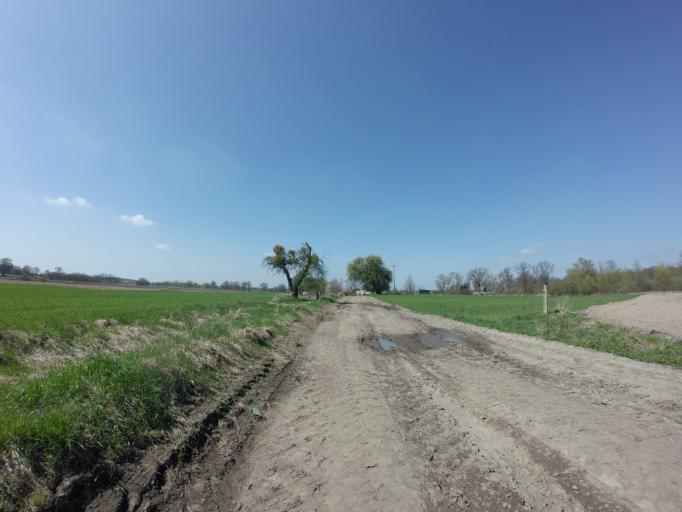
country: PL
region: West Pomeranian Voivodeship
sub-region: Powiat choszczenski
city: Choszczno
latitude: 53.1680
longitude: 15.4665
